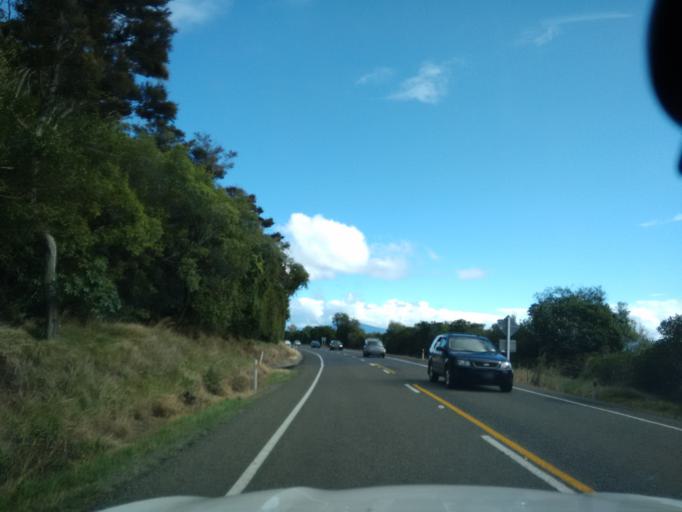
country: NZ
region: Waikato
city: Turangi
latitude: -38.8878
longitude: 175.9527
